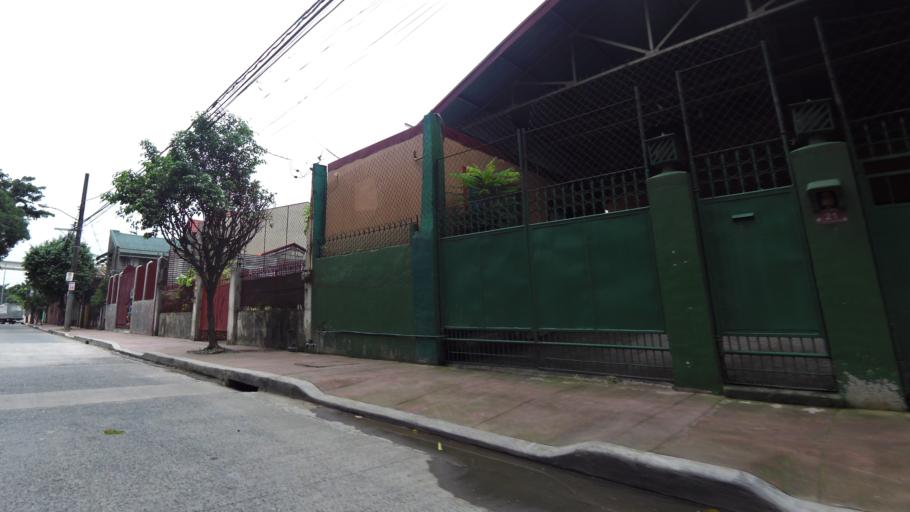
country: PH
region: Metro Manila
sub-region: Marikina
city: Calumpang
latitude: 14.6227
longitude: 121.1042
